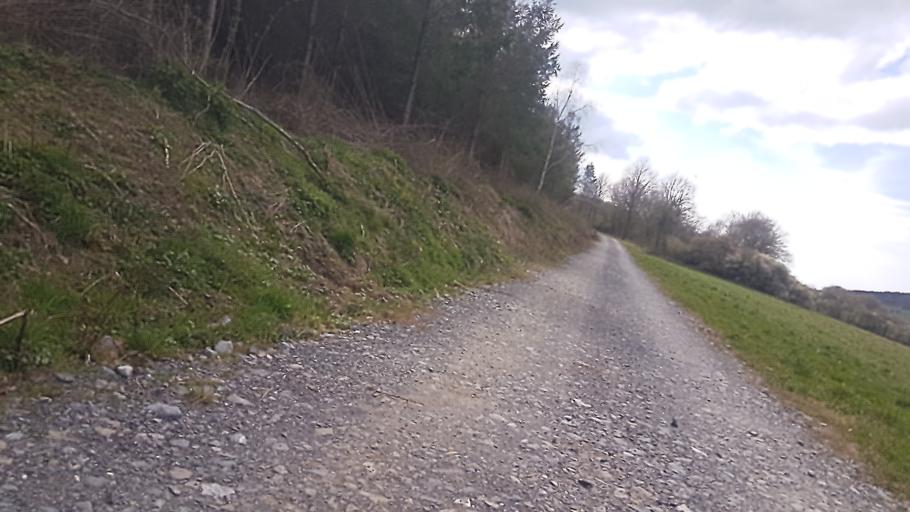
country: BE
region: Wallonia
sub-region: Province de Namur
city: Couvin
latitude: 50.0682
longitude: 4.5872
